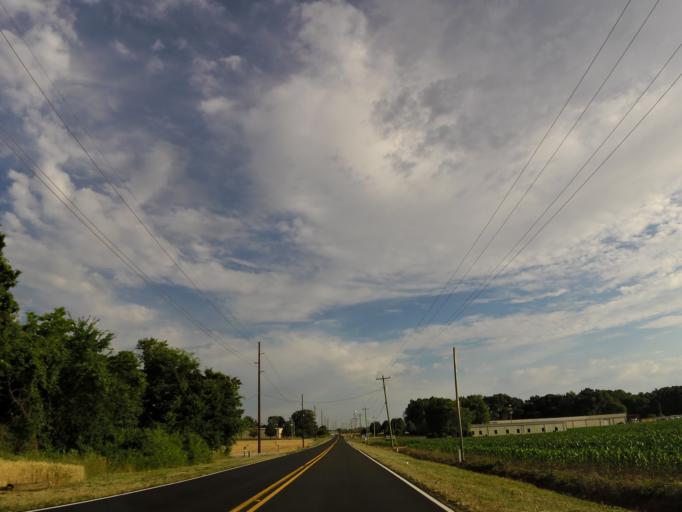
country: US
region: Alabama
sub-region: Morgan County
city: Trinity
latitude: 34.6185
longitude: -87.0522
